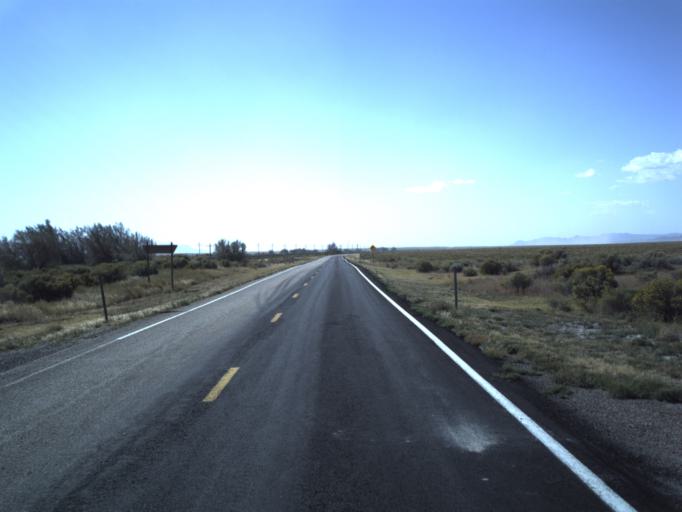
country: US
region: Utah
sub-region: Beaver County
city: Milford
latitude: 38.7168
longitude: -112.9689
